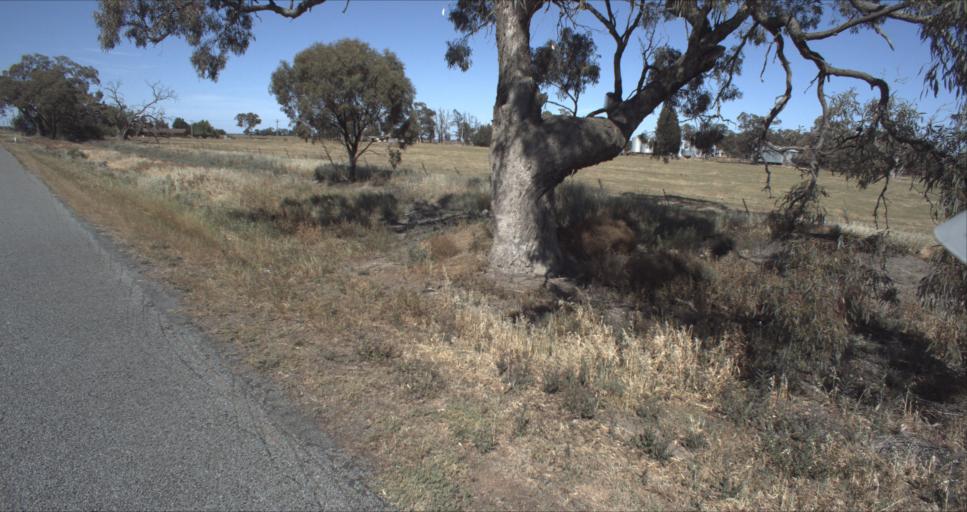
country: AU
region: New South Wales
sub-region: Leeton
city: Leeton
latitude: -34.5419
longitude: 146.3163
